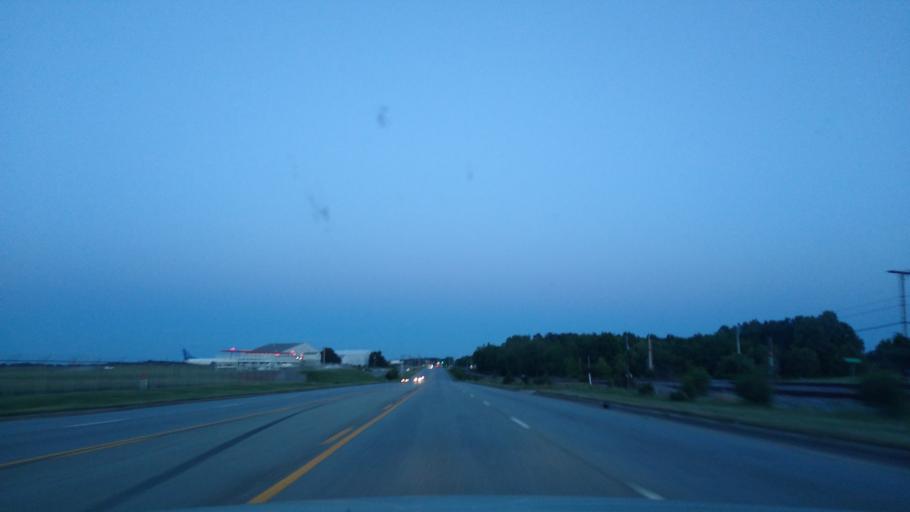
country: US
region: North Carolina
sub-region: Guilford County
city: Oak Ridge
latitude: 36.0904
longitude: -79.9480
